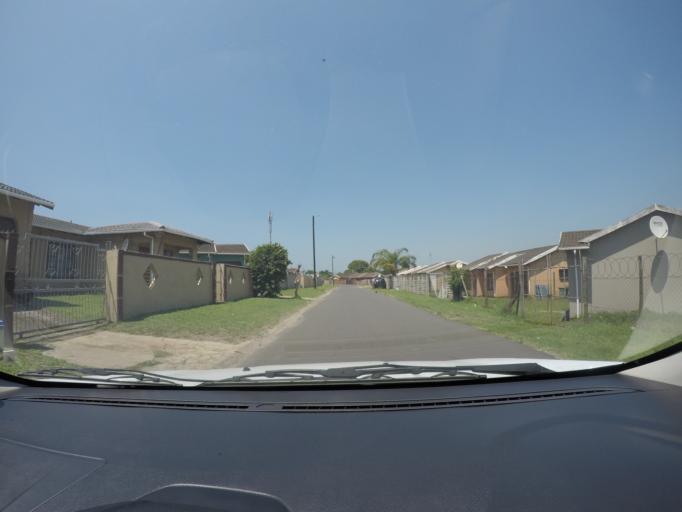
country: ZA
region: KwaZulu-Natal
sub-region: uThungulu District Municipality
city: eSikhawini
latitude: -28.8685
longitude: 31.9202
